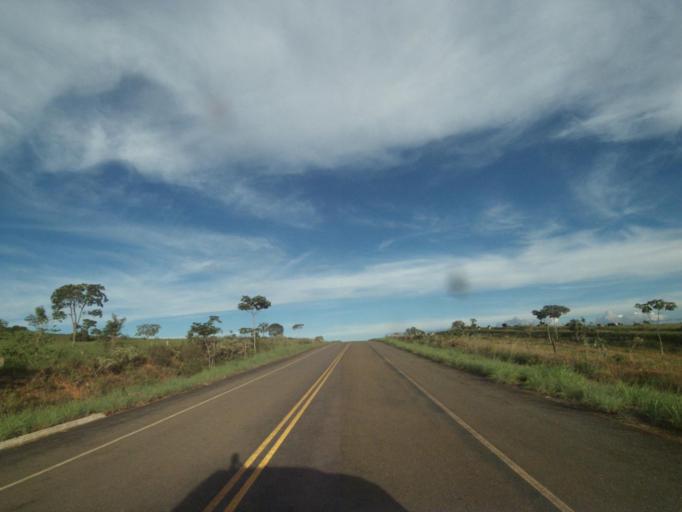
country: BR
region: Goias
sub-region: Jaragua
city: Jaragua
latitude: -15.8374
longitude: -49.3140
